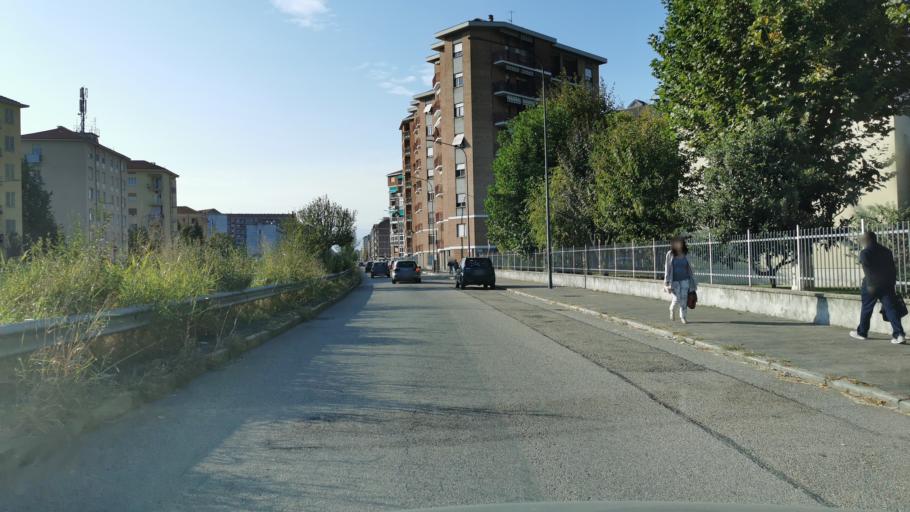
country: IT
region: Piedmont
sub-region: Provincia di Torino
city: Turin
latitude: 45.0923
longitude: 7.7102
